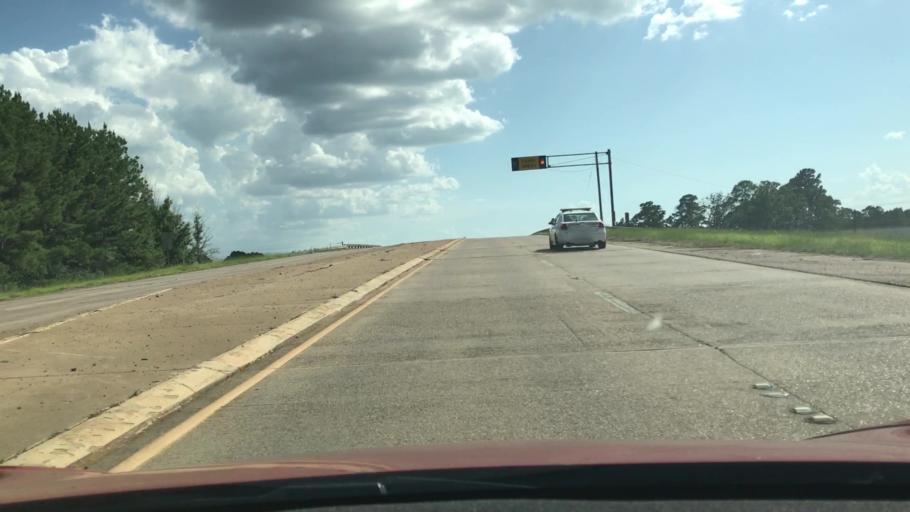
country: US
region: Louisiana
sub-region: Bossier Parish
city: Bossier City
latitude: 32.4018
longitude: -93.7342
